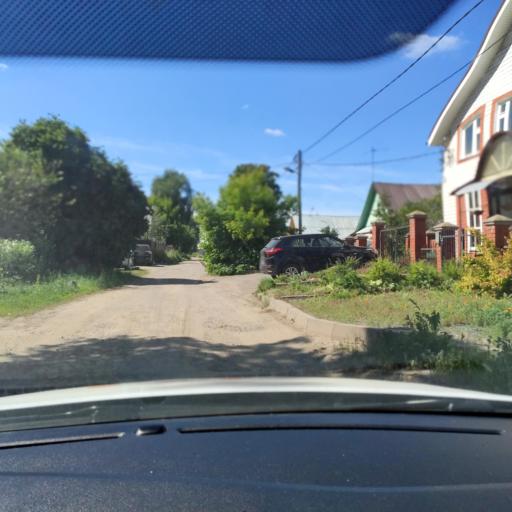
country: RU
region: Tatarstan
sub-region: Gorod Kazan'
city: Kazan
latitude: 55.8430
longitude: 49.2001
